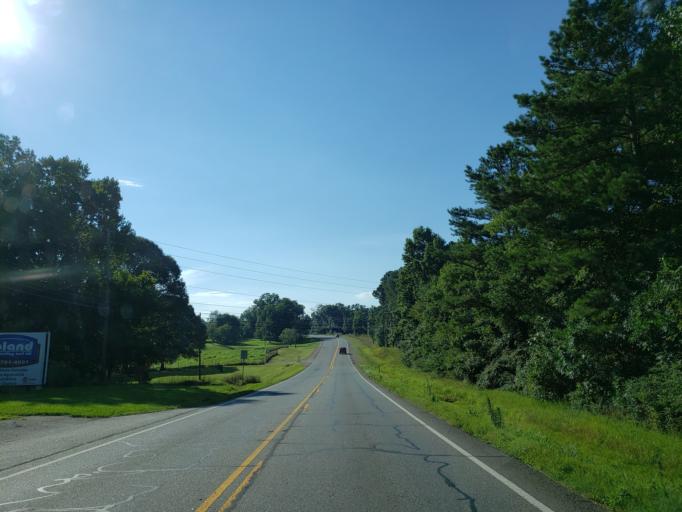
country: US
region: Georgia
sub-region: Cherokee County
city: Ball Ground
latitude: 34.2502
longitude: -84.3096
